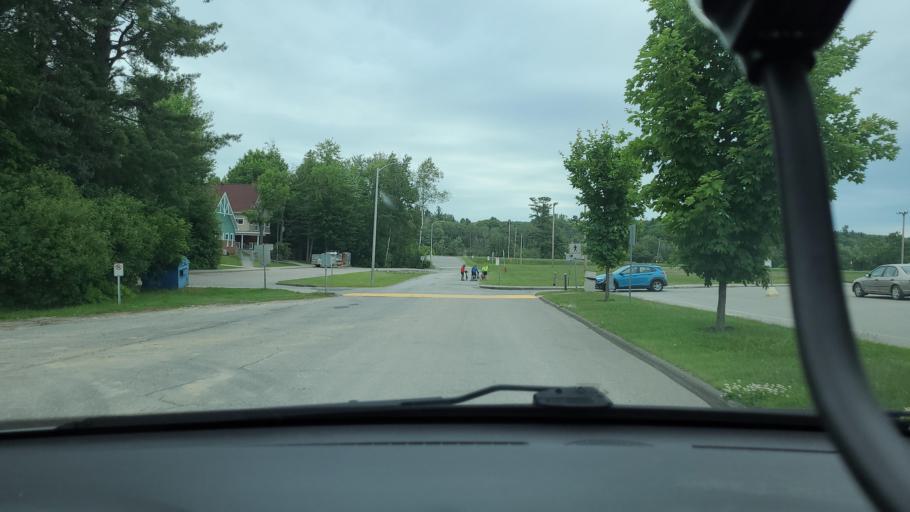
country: CA
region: Quebec
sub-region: Estrie
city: Sherbrooke
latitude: 45.3644
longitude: -71.8432
